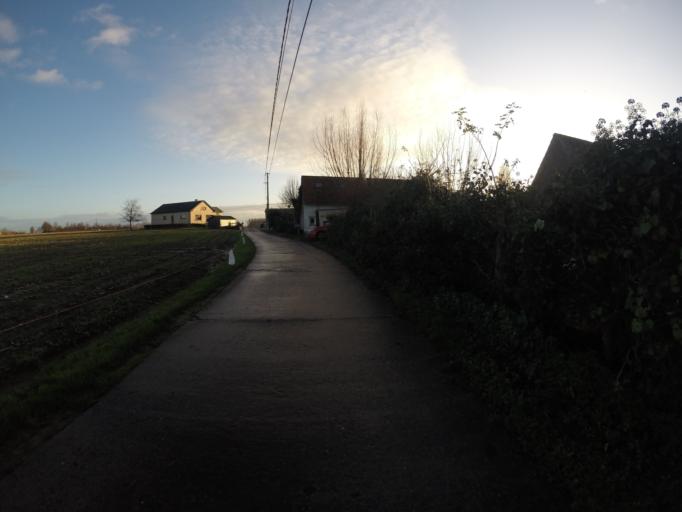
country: BE
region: Flanders
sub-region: Provincie Oost-Vlaanderen
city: Nevele
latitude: 51.0388
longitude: 3.4919
